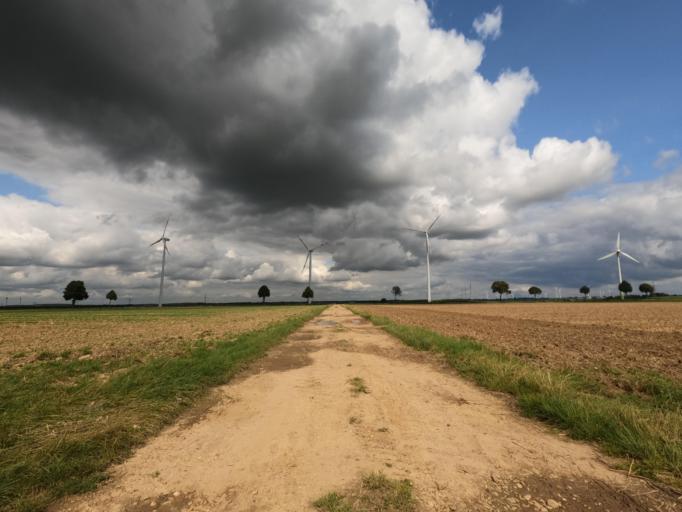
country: DE
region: North Rhine-Westphalia
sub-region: Regierungsbezirk Koln
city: Linnich
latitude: 50.9864
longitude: 6.2299
